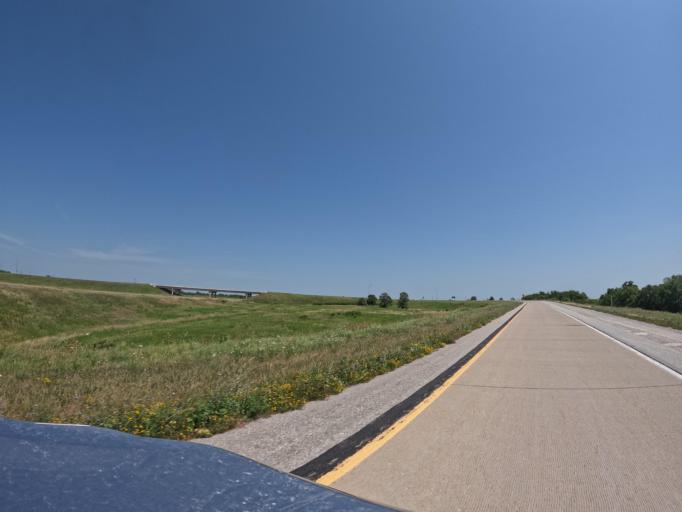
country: US
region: Iowa
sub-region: Henry County
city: Mount Pleasant
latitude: 40.9353
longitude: -91.5342
